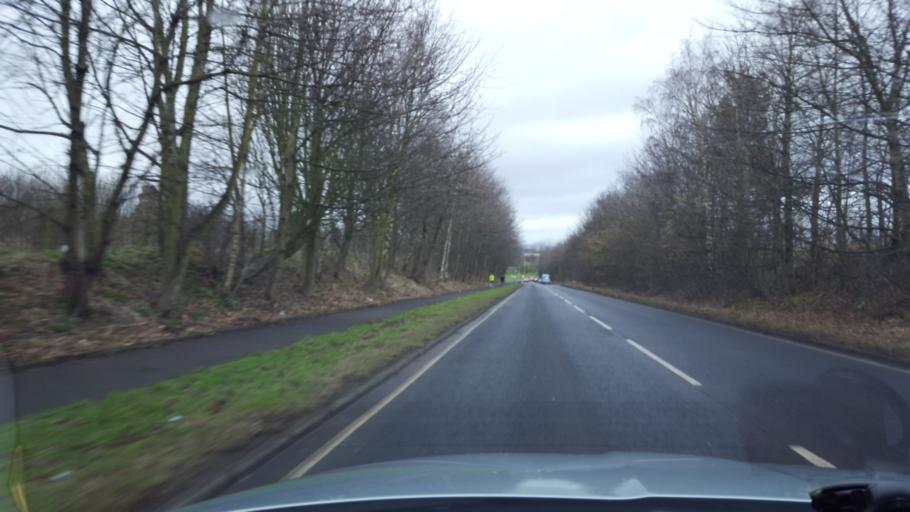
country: GB
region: Scotland
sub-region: Edinburgh
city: Currie
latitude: 55.9093
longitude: -3.3120
